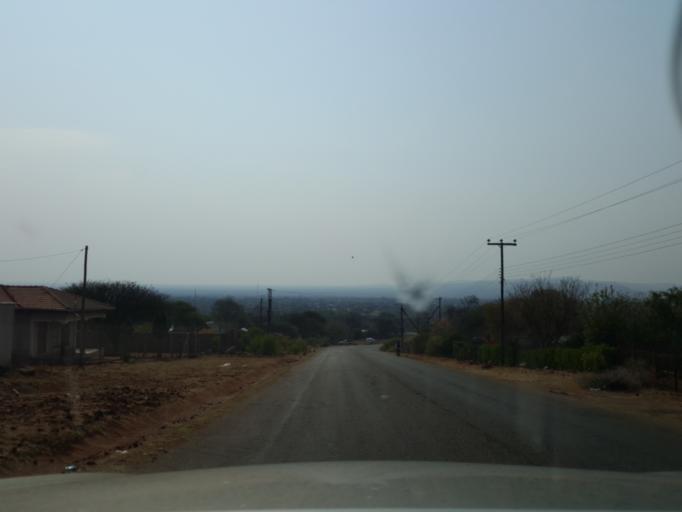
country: BW
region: South East
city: Lobatse
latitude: -25.2856
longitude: 25.8936
